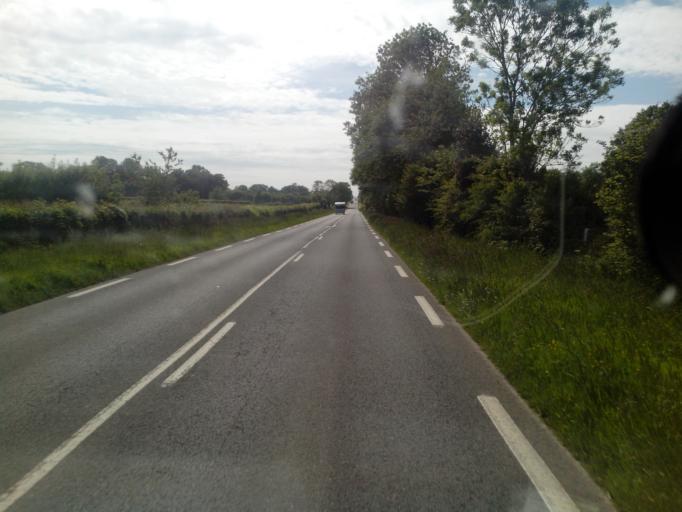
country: FR
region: Lower Normandy
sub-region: Departement du Calvados
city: Touques
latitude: 49.2576
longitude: 0.0811
